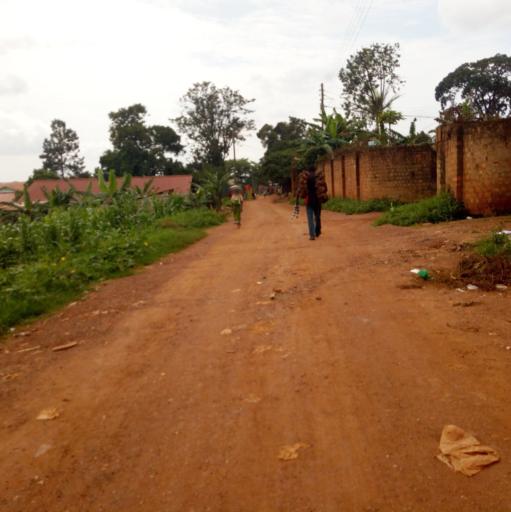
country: UG
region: Central Region
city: Kampala Central Division
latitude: 0.3406
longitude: 32.5599
